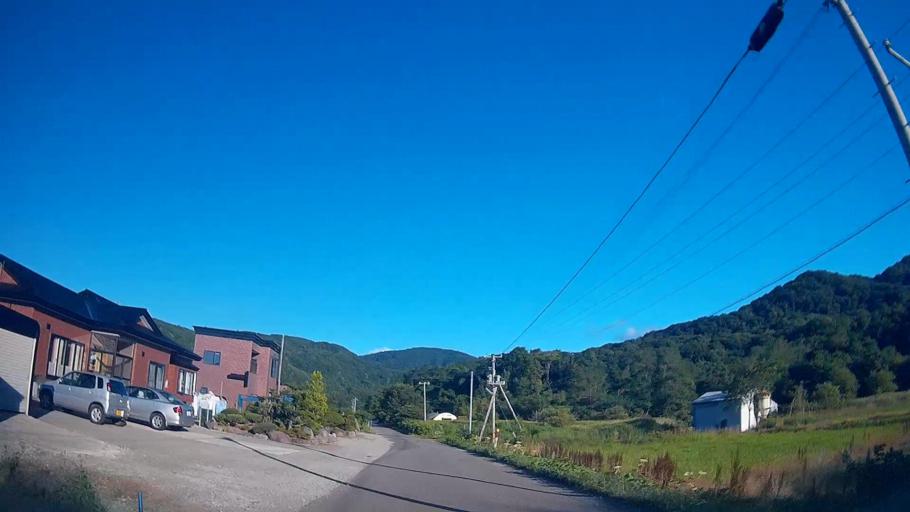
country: JP
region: Hokkaido
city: Iwanai
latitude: 42.6829
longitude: 140.0108
